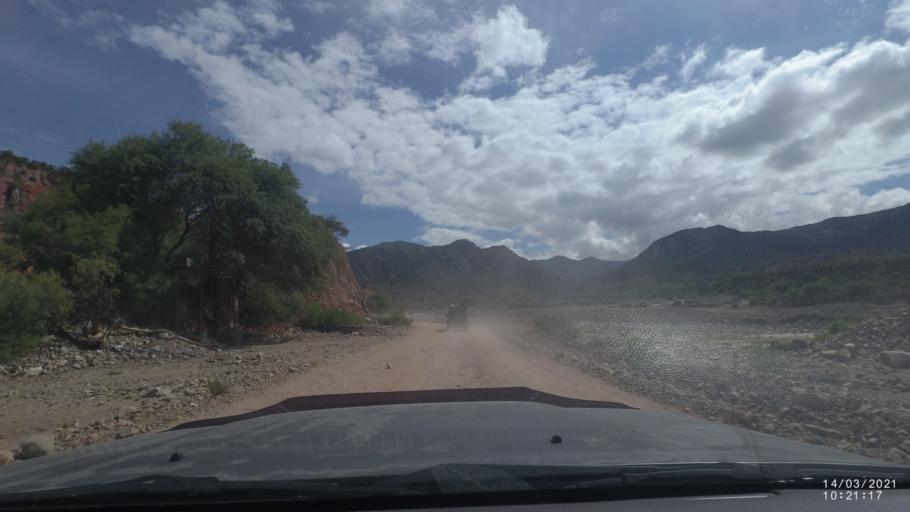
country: BO
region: Cochabamba
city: Cliza
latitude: -17.9257
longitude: -65.8724
